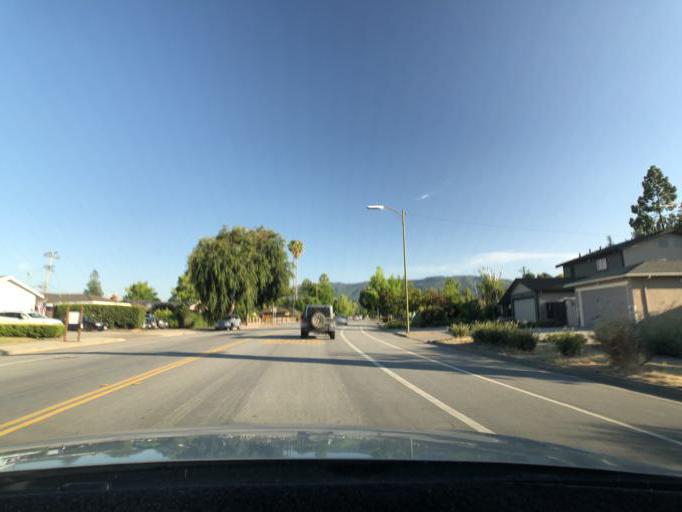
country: US
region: California
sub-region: Santa Clara County
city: Cambrian Park
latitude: 37.2592
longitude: -121.9219
